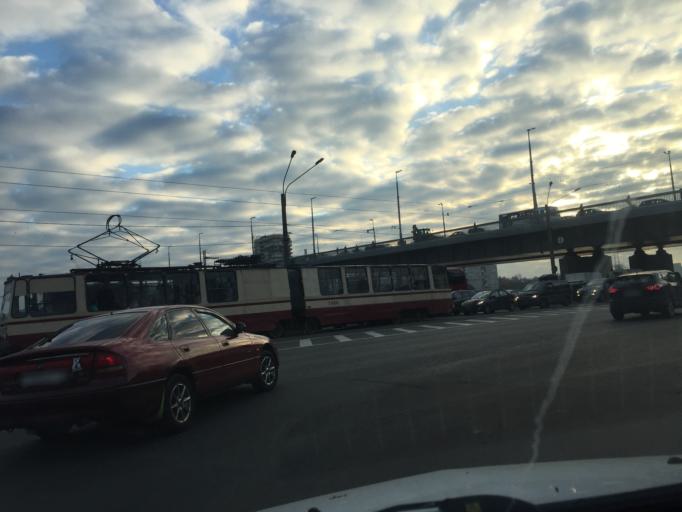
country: RU
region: St.-Petersburg
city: Obukhovo
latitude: 59.8777
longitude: 30.4497
